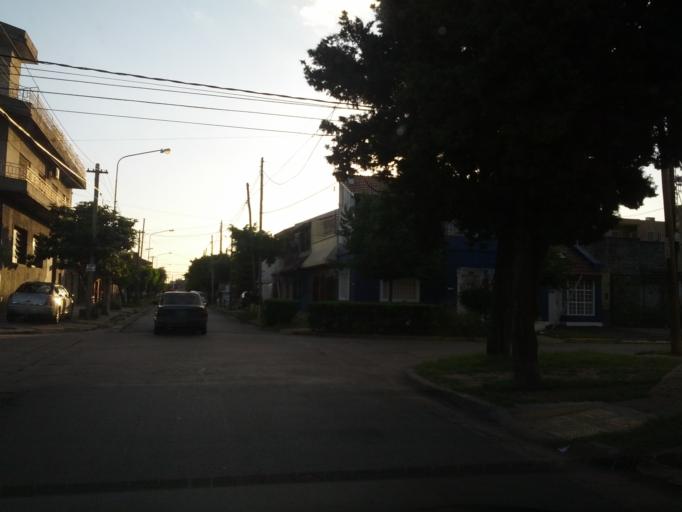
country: AR
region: Buenos Aires
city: San Justo
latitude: -34.6564
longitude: -58.5434
